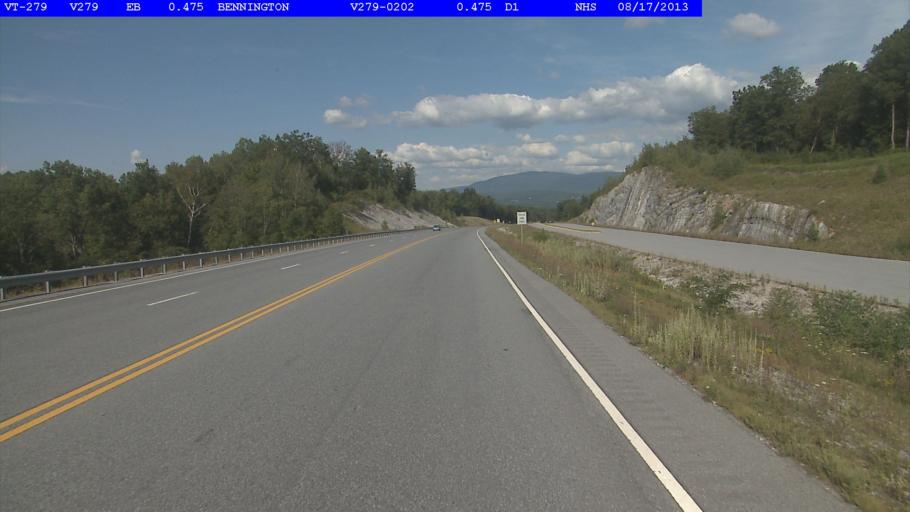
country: US
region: Vermont
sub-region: Bennington County
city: North Bennington
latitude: 42.8969
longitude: -73.2697
